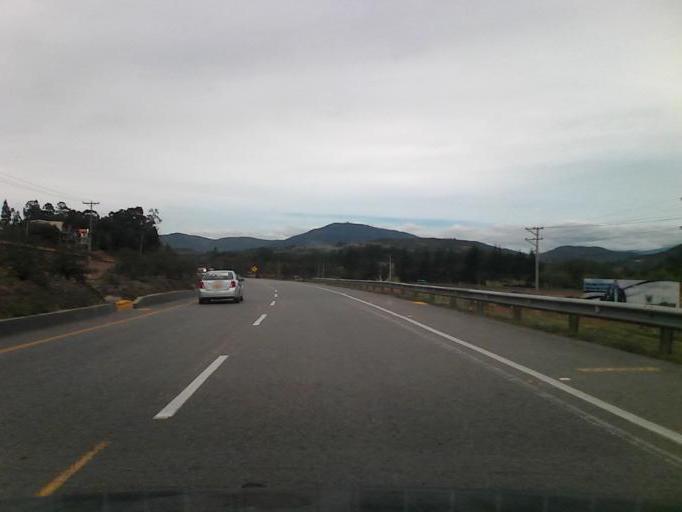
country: CO
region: Boyaca
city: Duitama
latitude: 5.7904
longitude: -73.0522
